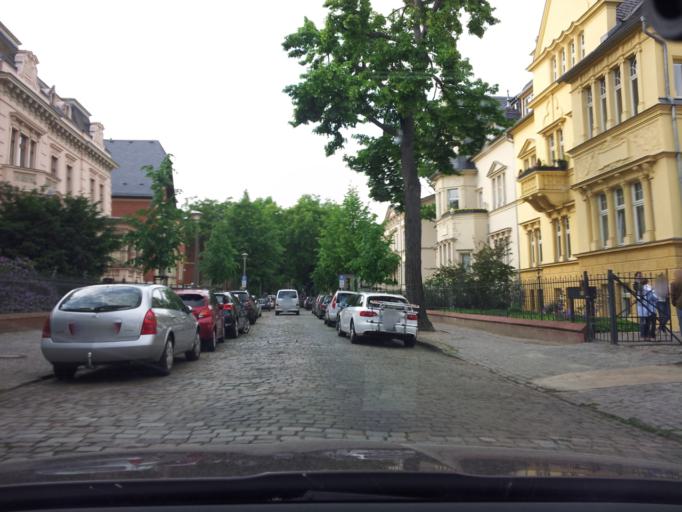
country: DE
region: Brandenburg
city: Potsdam
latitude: 52.4047
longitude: 13.0622
